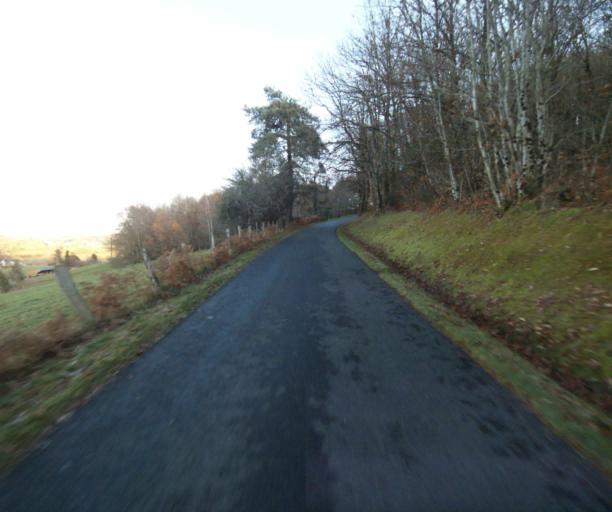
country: FR
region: Limousin
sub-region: Departement de la Correze
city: Laguenne
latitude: 45.2327
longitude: 1.8231
